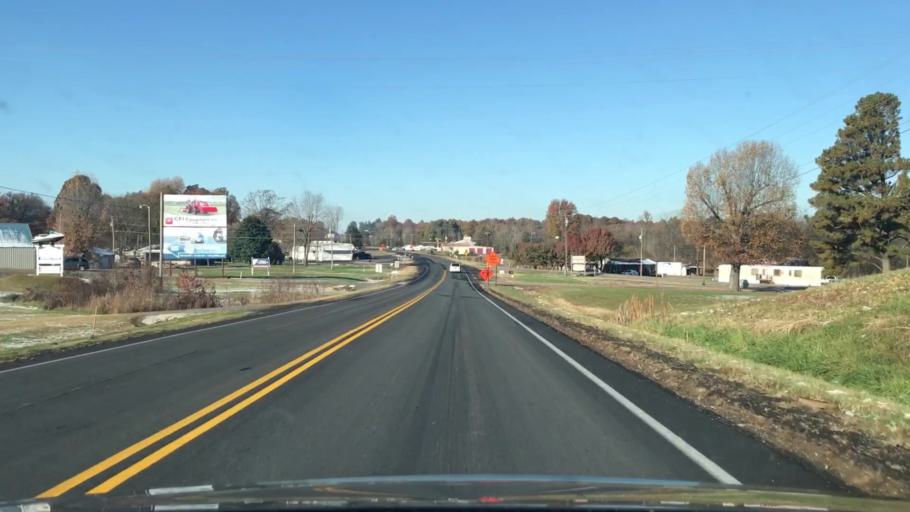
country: US
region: Kentucky
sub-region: Livingston County
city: Ledbetter
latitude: 37.0062
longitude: -88.4275
